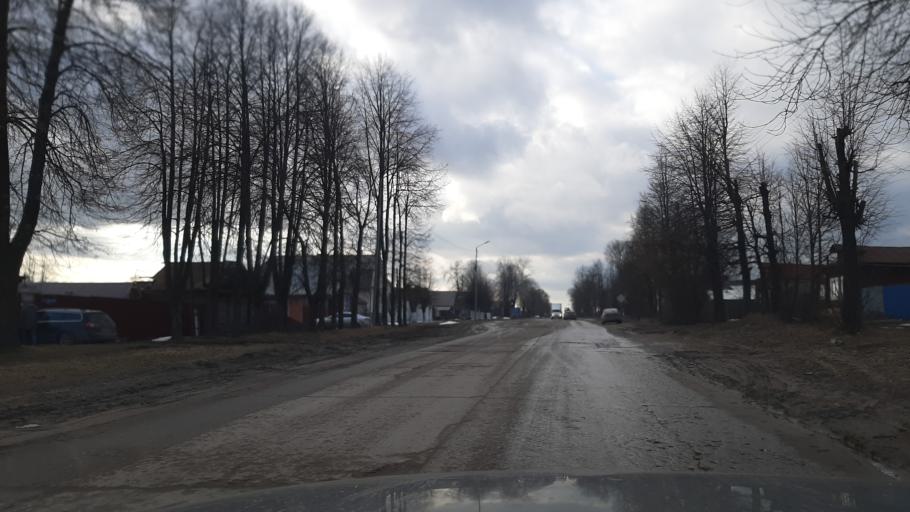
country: RU
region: Ivanovo
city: Teykovo
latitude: 56.8592
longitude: 40.5360
